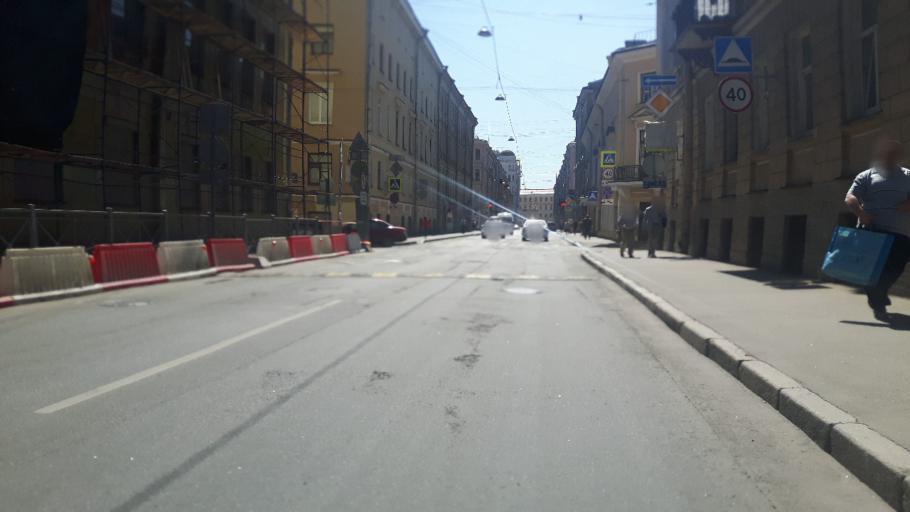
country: RU
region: St.-Petersburg
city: Saint Petersburg
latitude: 59.9297
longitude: 30.3044
